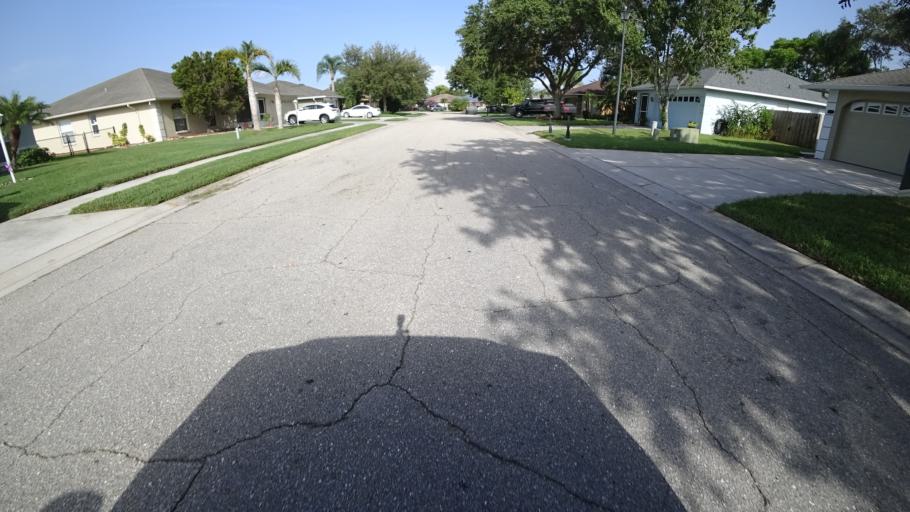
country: US
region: Florida
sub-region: Sarasota County
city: Desoto Lakes
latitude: 27.4247
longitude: -82.4732
